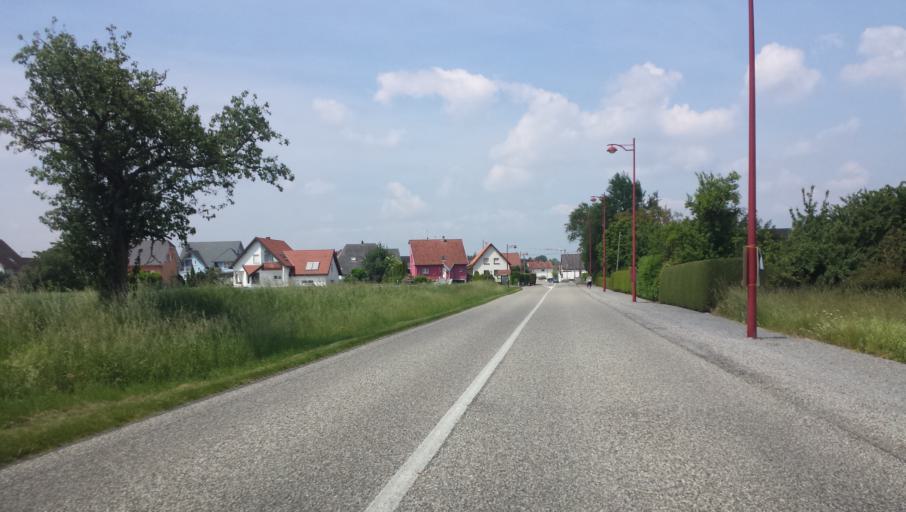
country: DE
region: Rheinland-Pfalz
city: Scheibenhardt
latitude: 48.9763
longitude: 8.1417
